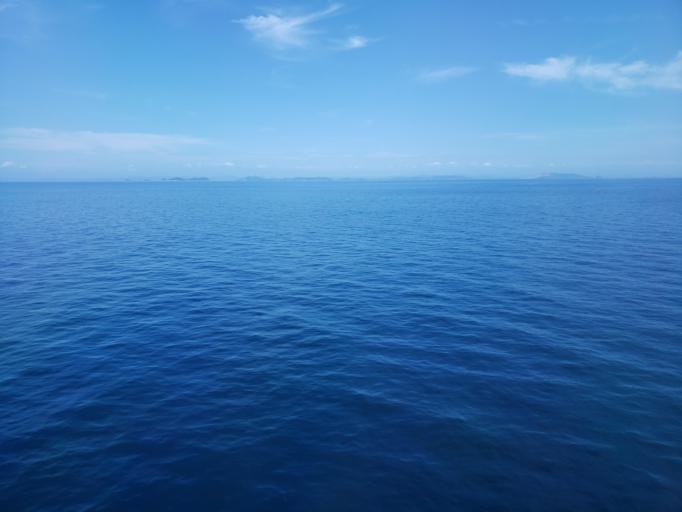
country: JP
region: Hyogo
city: Fukura
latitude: 34.4940
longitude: 134.5697
